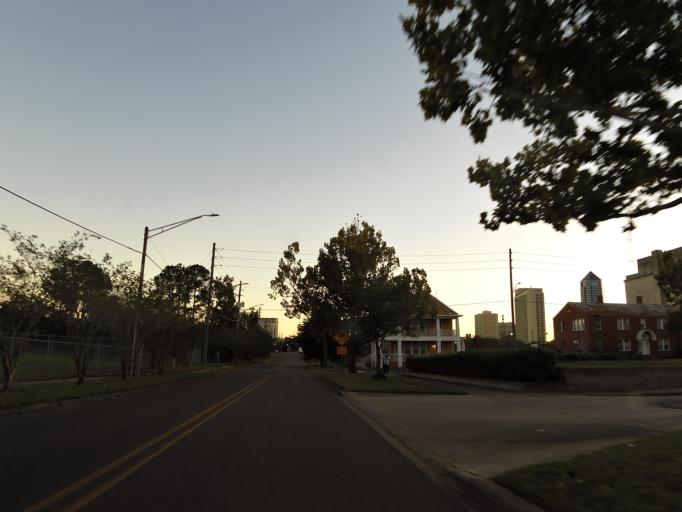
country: US
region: Florida
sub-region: Duval County
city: Jacksonville
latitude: 30.3354
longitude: -81.6520
